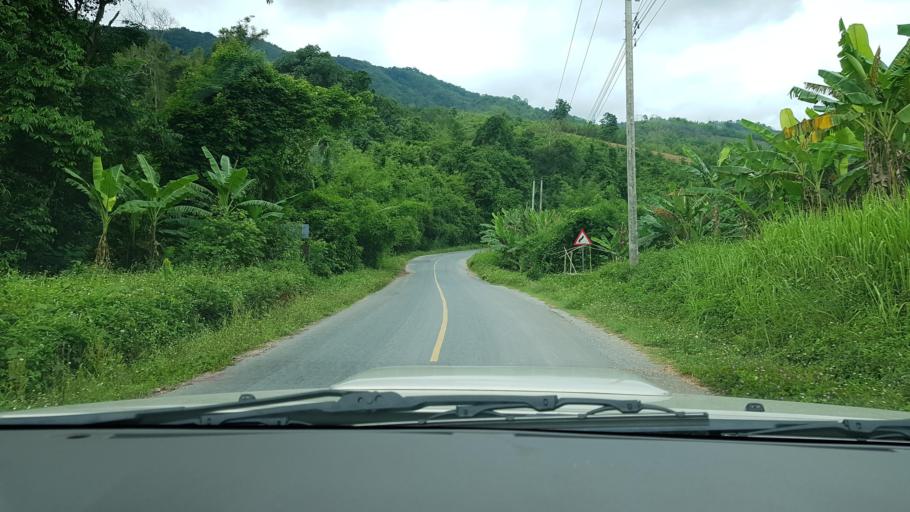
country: LA
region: Loungnamtha
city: Muang Nale
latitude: 20.3810
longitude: 101.7406
